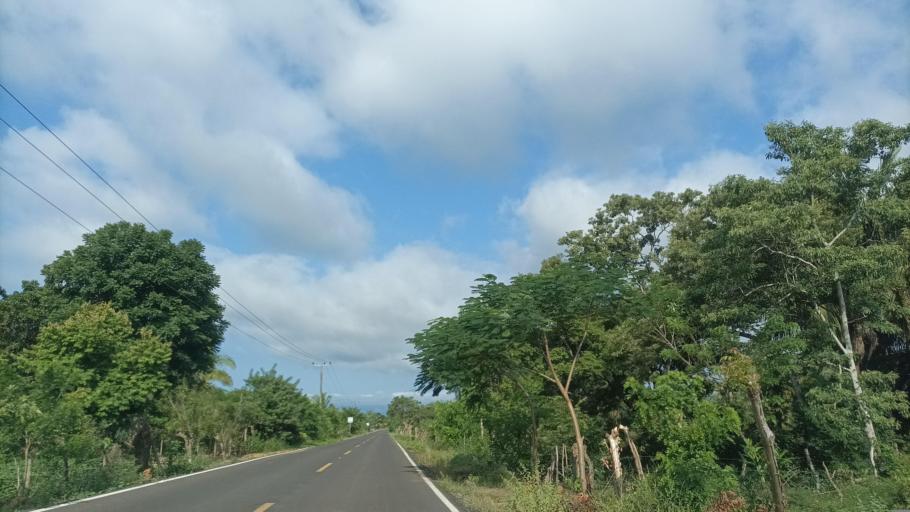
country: MX
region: Veracruz
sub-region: Chinameca
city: Chacalapa
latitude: 18.1671
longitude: -94.6632
